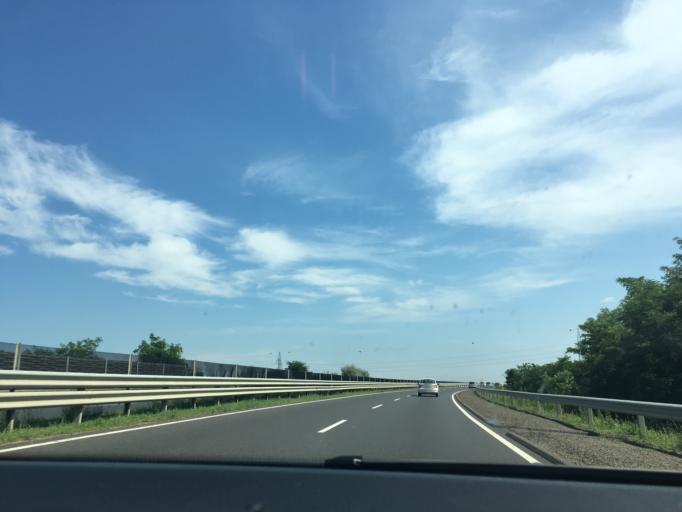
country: HU
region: Szabolcs-Szatmar-Bereg
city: Nyiregyhaza
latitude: 47.9103
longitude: 21.7140
